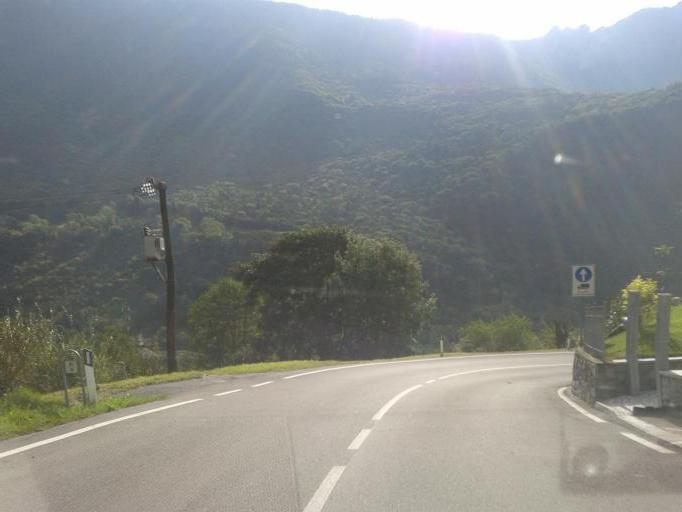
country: IT
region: Trentino-Alto Adige
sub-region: Provincia di Trento
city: Cimego
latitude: 45.9142
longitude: 10.6162
